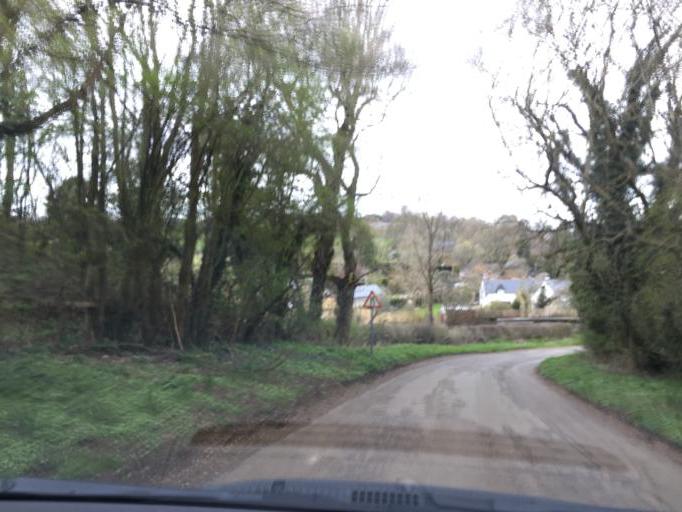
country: GB
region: England
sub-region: Oxfordshire
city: Hanwell
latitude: 52.0868
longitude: -1.3923
